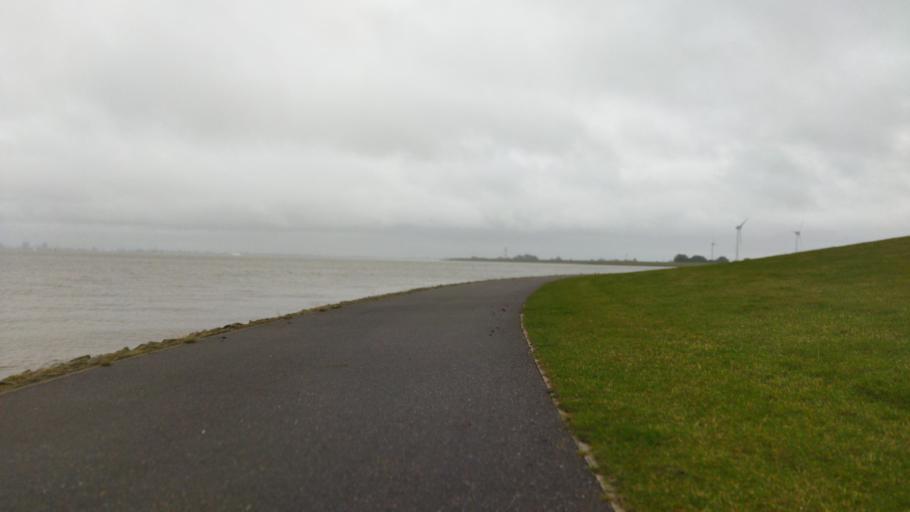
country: NL
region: Groningen
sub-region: Gemeente Delfzijl
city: Delfzijl
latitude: 53.3345
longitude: 7.0578
